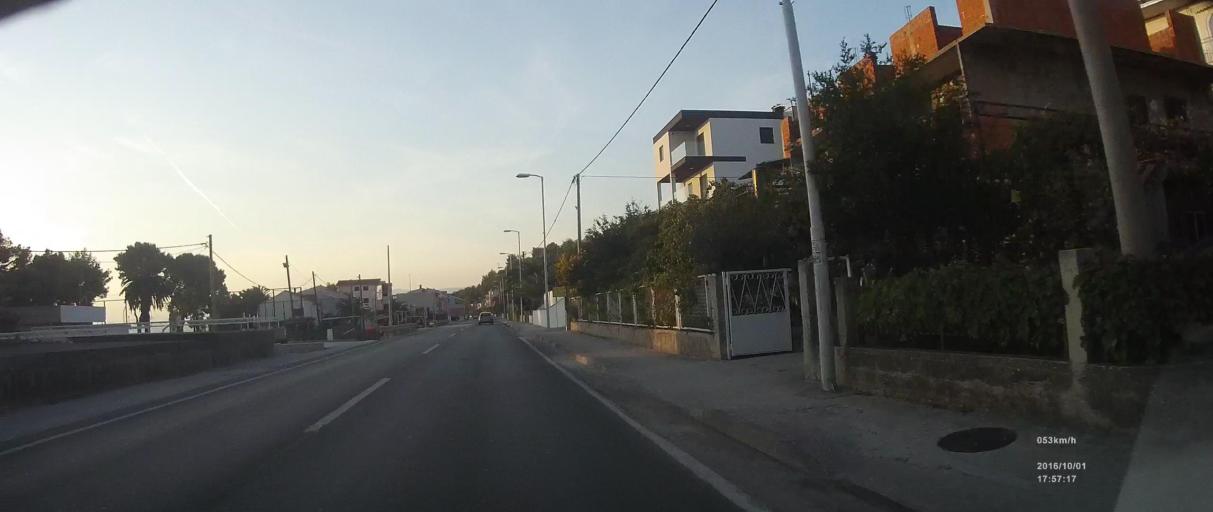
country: HR
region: Splitsko-Dalmatinska
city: Srinjine
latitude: 43.4690
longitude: 16.5758
